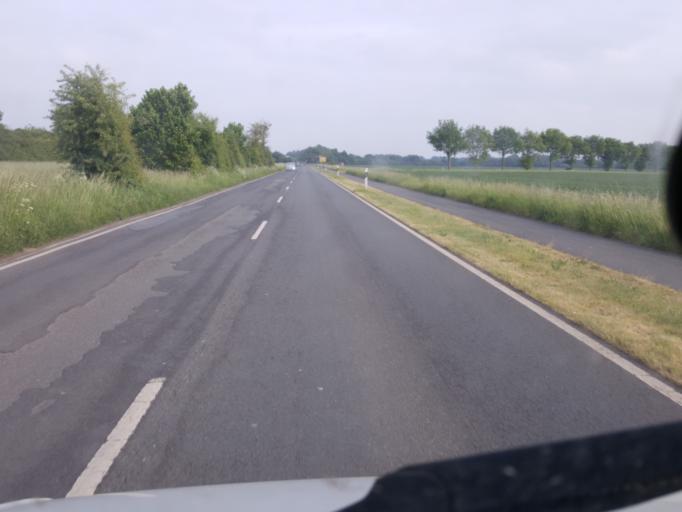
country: DE
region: Lower Saxony
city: Nienburg
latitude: 52.6499
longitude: 9.1916
